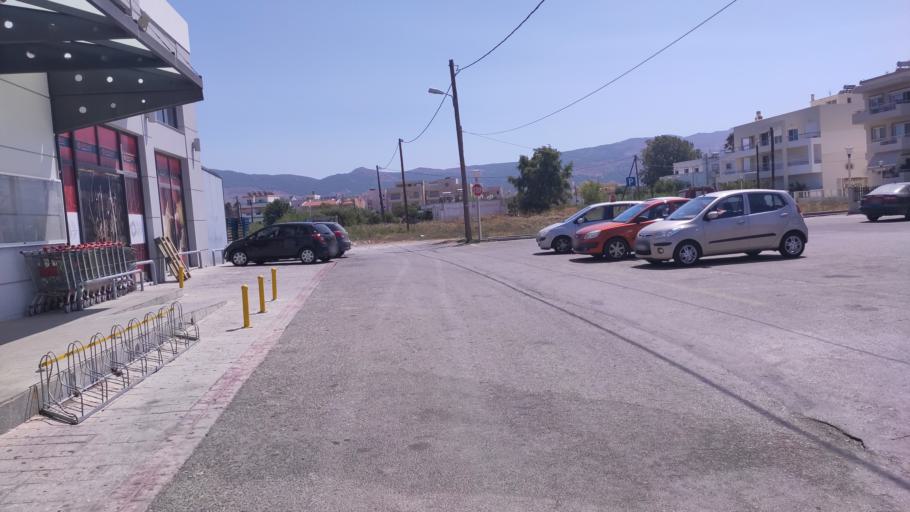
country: GR
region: South Aegean
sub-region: Nomos Dodekanisou
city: Kos
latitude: 36.8995
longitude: 27.2802
